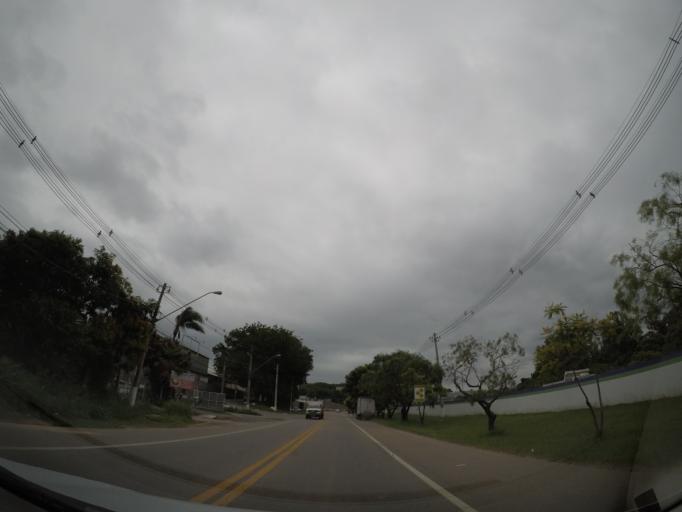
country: BR
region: Sao Paulo
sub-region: Louveira
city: Louveira
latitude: -23.0993
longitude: -46.9461
